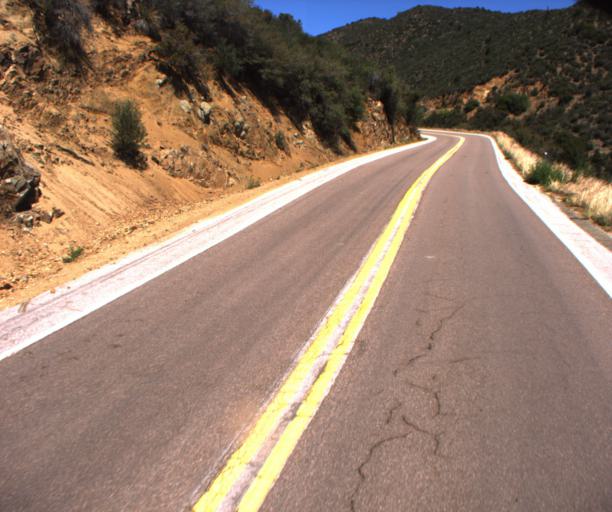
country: US
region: Arizona
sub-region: Yavapai County
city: Prescott
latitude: 34.4558
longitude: -112.5231
